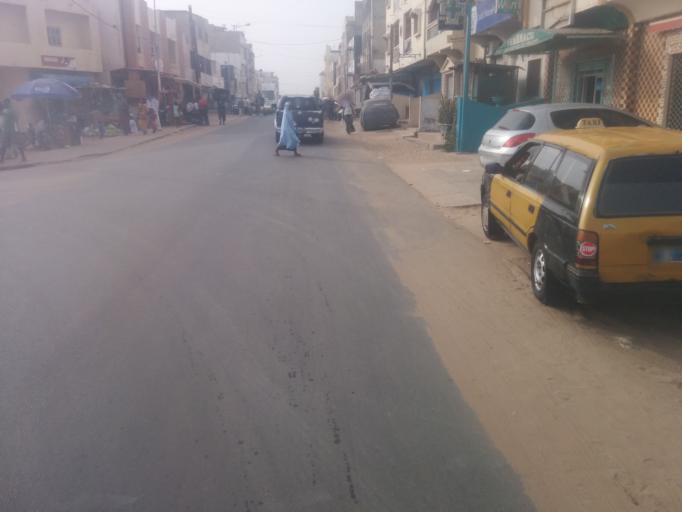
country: SN
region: Dakar
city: Grand Dakar
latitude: 14.7555
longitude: -17.4471
